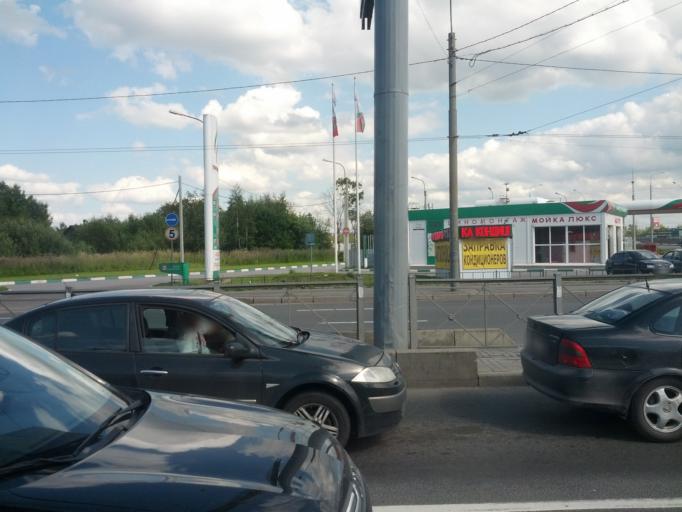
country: RU
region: Leningrad
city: Rybatskoye
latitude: 59.8858
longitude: 30.4892
